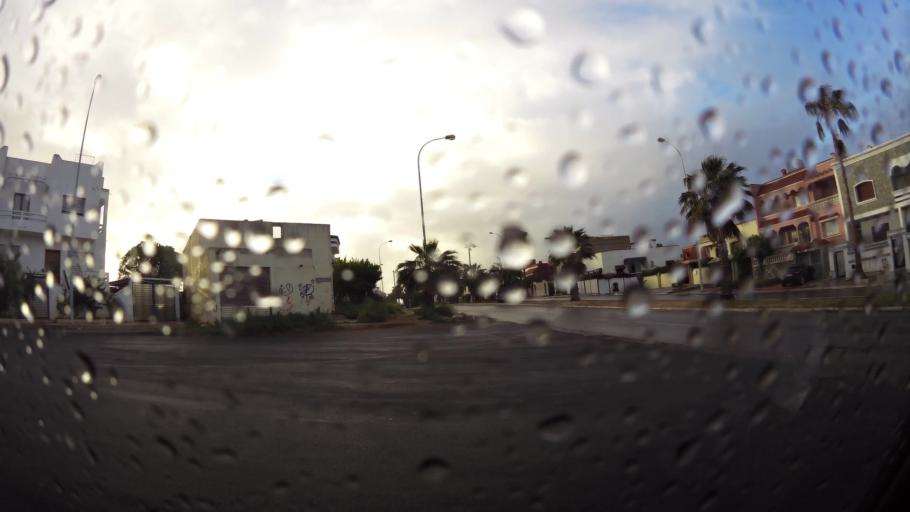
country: MA
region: Doukkala-Abda
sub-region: El-Jadida
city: El Jadida
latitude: 33.2287
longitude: -8.4965
